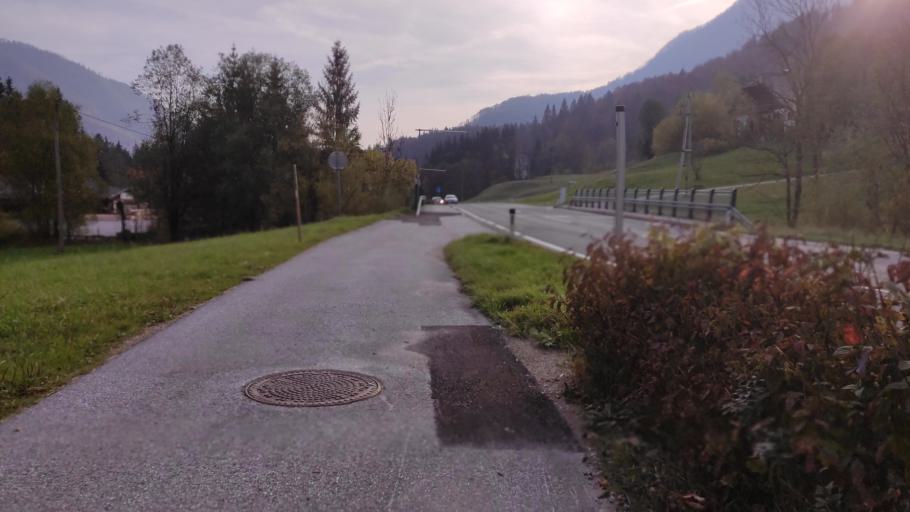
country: AT
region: Salzburg
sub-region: Politischer Bezirk Salzburg-Umgebung
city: Ebenau
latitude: 47.7767
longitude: 13.1812
